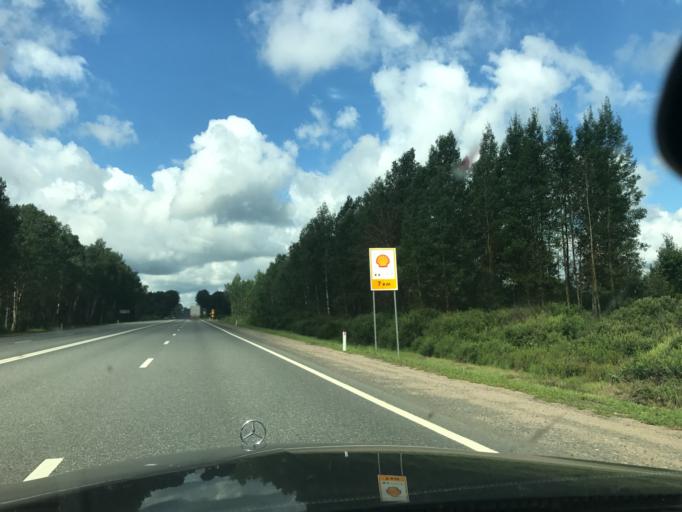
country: RU
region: Smolensk
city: Golynki
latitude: 54.7030
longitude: 31.1969
